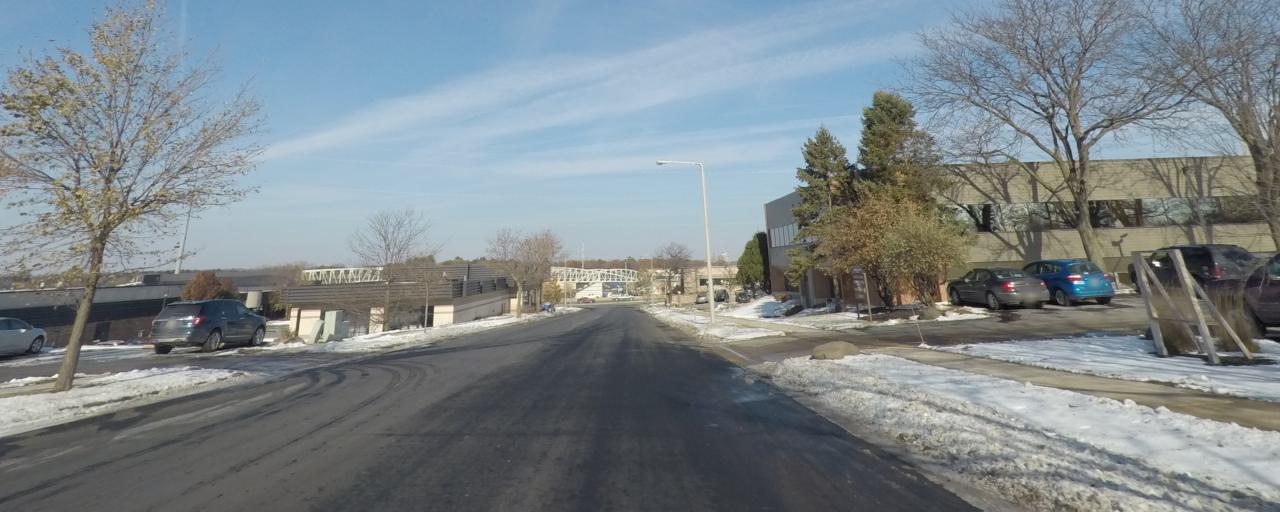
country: US
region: Wisconsin
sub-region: Dane County
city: Madison
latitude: 43.0331
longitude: -89.4149
